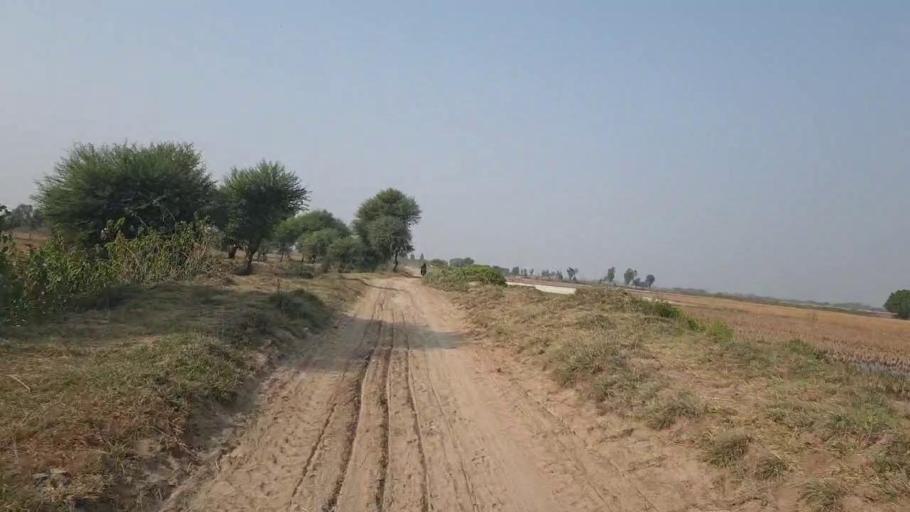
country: PK
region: Sindh
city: Tando Muhammad Khan
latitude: 25.0717
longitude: 68.3562
